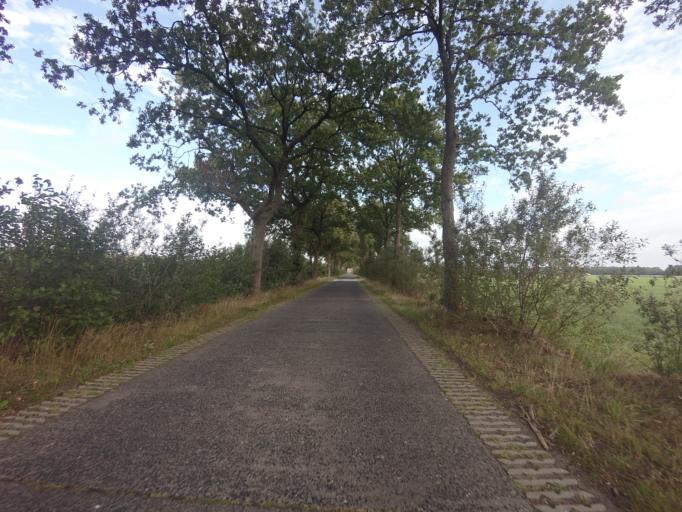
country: NL
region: Friesland
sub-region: Gemeente Heerenveen
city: Jubbega
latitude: 52.9820
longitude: 6.1453
